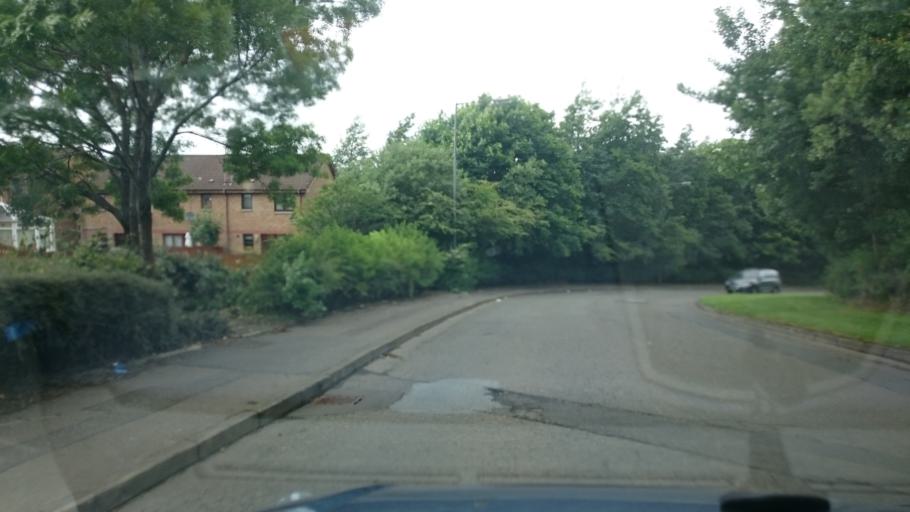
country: GB
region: Scotland
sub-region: Falkirk
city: Bonnybridge
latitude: 55.9990
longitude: -3.8848
